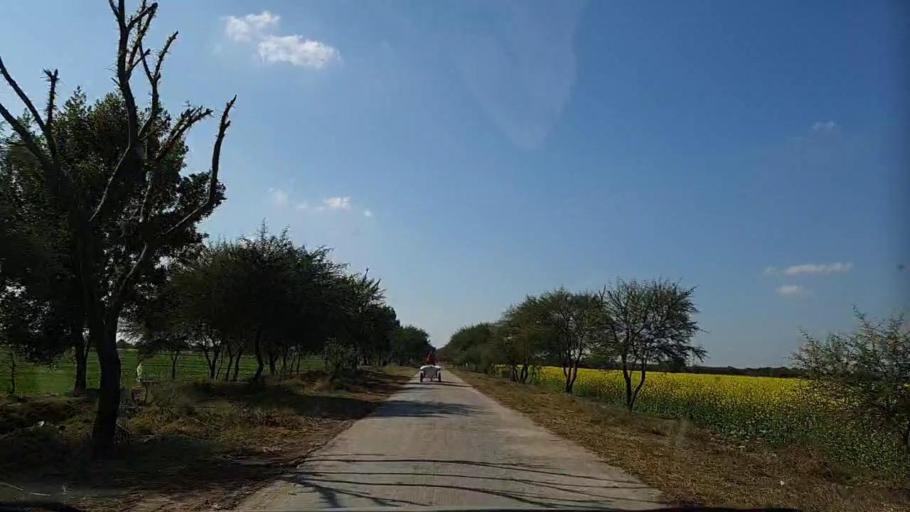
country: PK
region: Sindh
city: Pithoro
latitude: 25.6661
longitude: 69.4612
